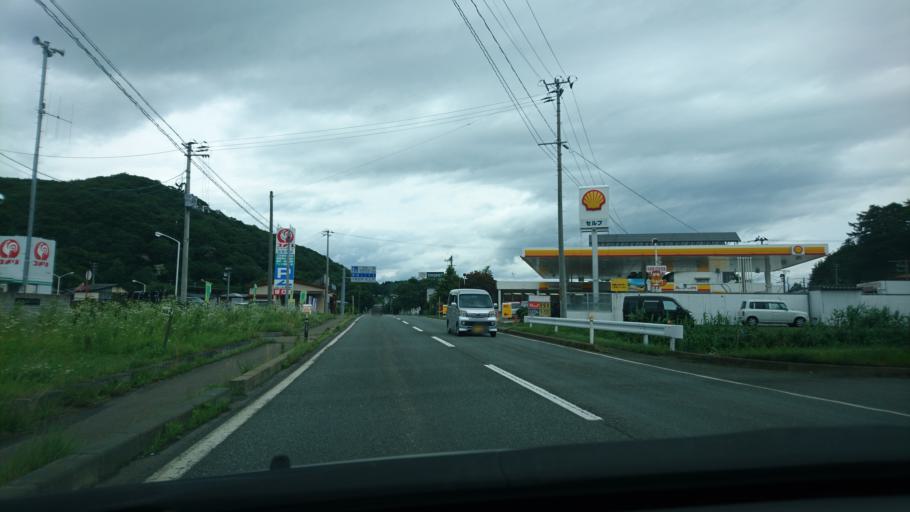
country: JP
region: Iwate
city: Morioka-shi
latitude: 39.9515
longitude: 141.2169
